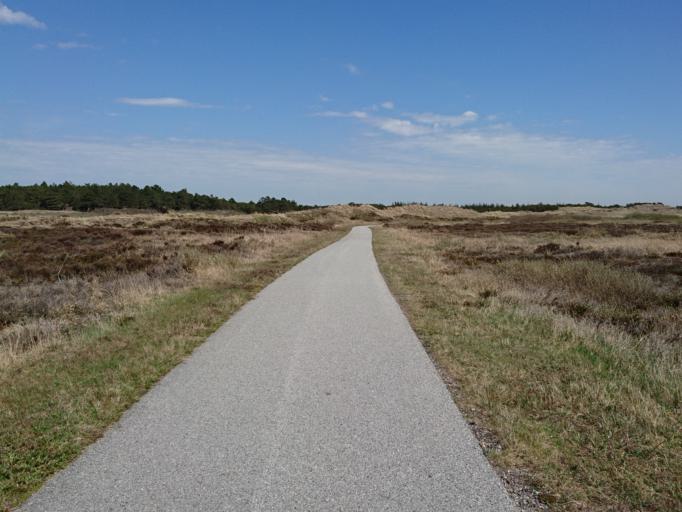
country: DK
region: North Denmark
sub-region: Frederikshavn Kommune
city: Skagen
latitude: 57.6910
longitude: 10.5021
